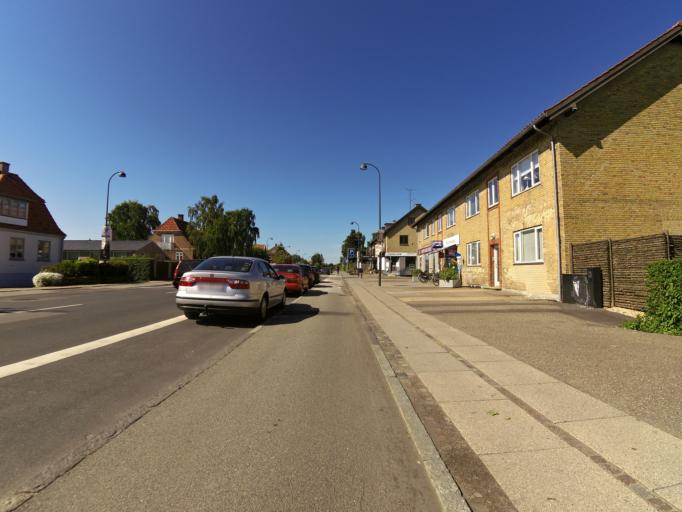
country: DK
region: Capital Region
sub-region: Lyngby-Tarbaek Kommune
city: Kongens Lyngby
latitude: 55.7408
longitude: 12.5237
